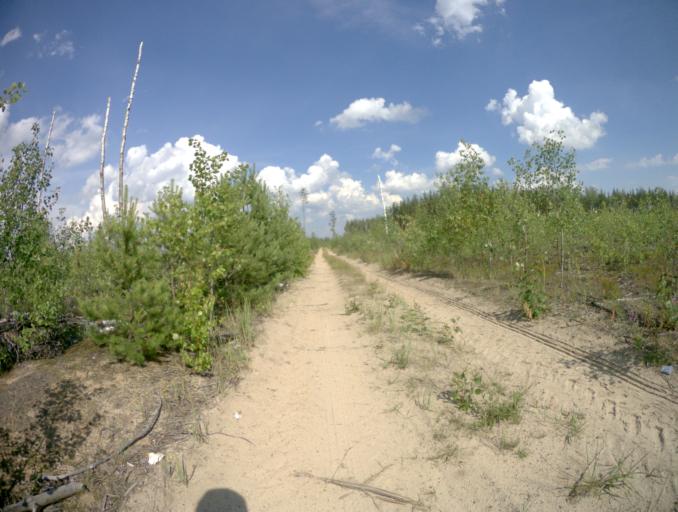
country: RU
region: Ivanovo
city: Talitsy
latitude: 56.5325
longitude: 42.2409
